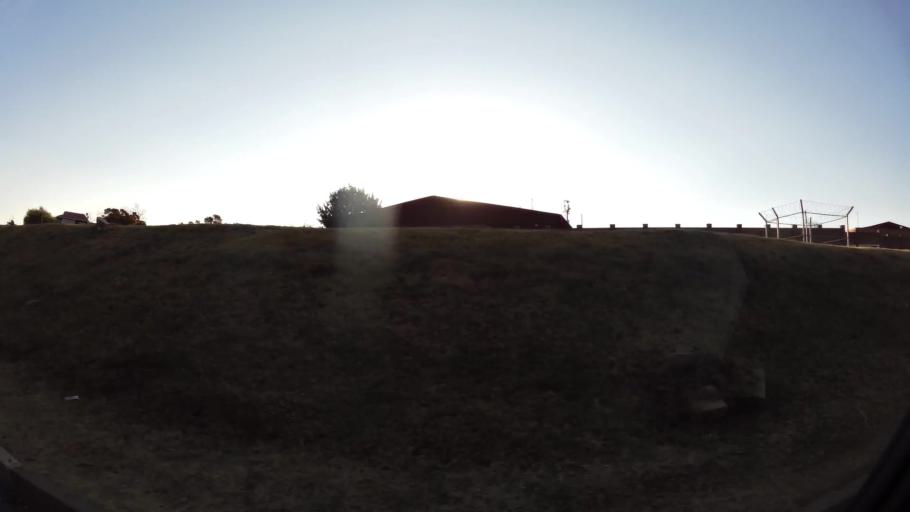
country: ZA
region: Gauteng
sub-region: City of Johannesburg Metropolitan Municipality
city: Midrand
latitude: -25.9901
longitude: 28.1213
